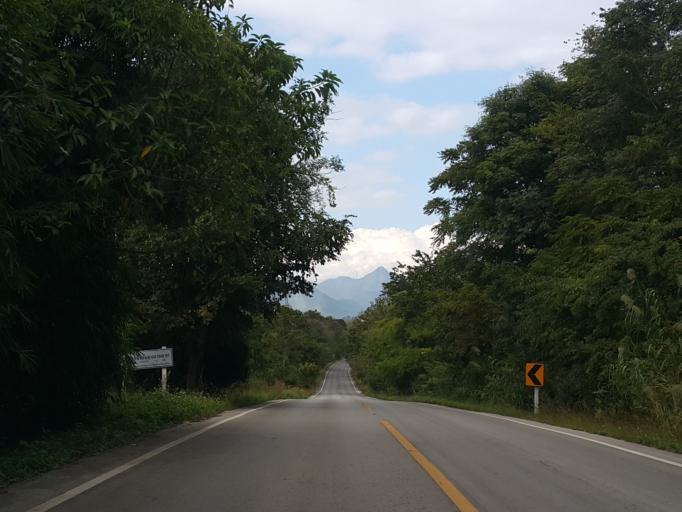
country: TH
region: Lampang
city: Chae Hom
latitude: 18.6100
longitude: 99.4836
